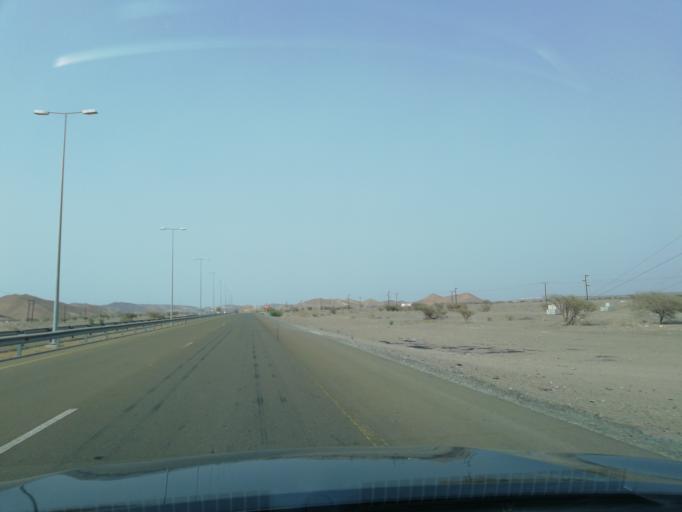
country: OM
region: Al Batinah
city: Al Liwa'
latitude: 24.3575
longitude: 56.5266
